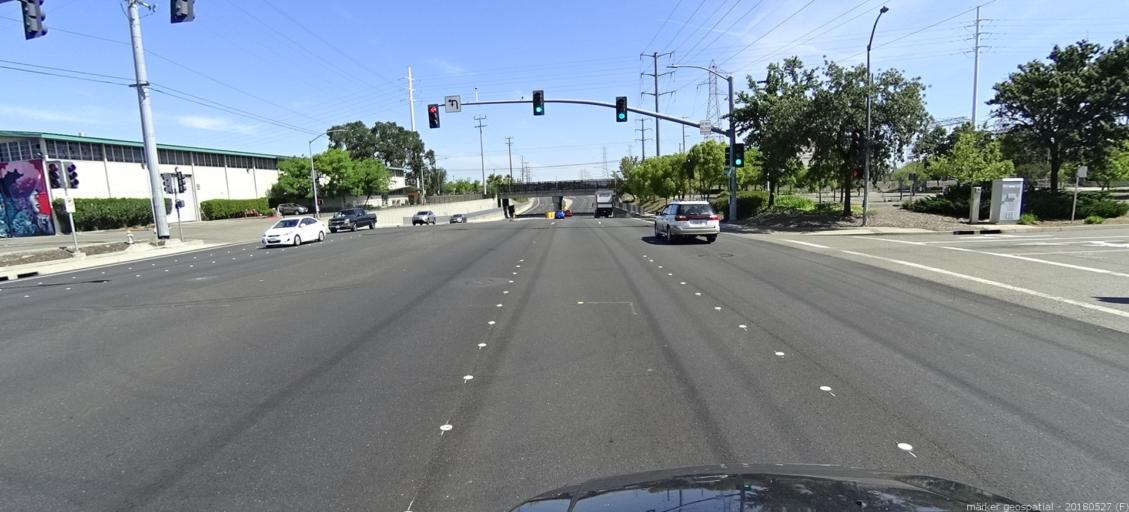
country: US
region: California
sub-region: Sacramento County
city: Rosemont
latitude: 38.5462
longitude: -121.4089
